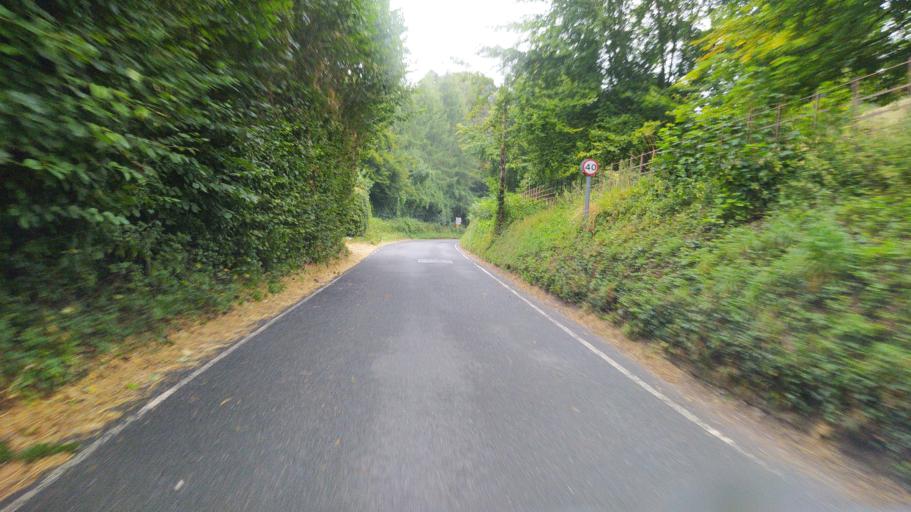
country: GB
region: England
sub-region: Wiltshire
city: Ansty
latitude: 50.9569
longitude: -2.0776
